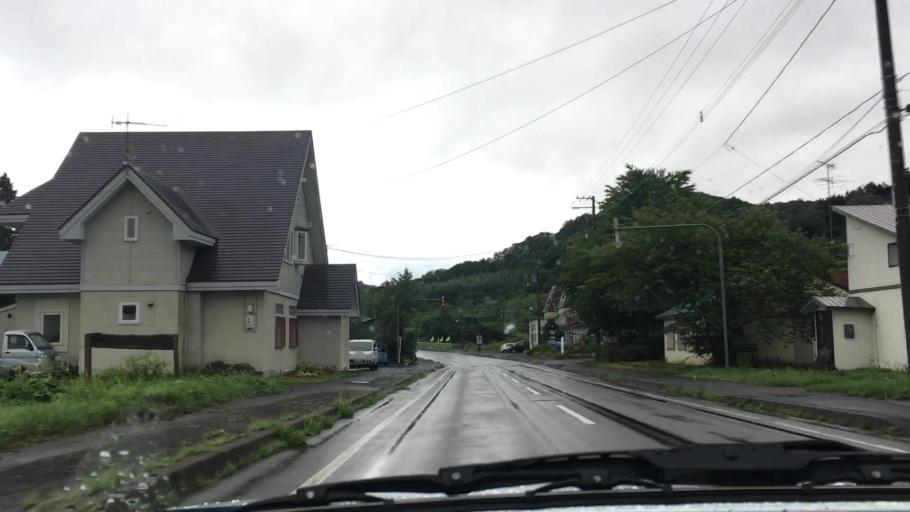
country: JP
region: Hokkaido
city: Niseko Town
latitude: 42.6461
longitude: 140.7335
